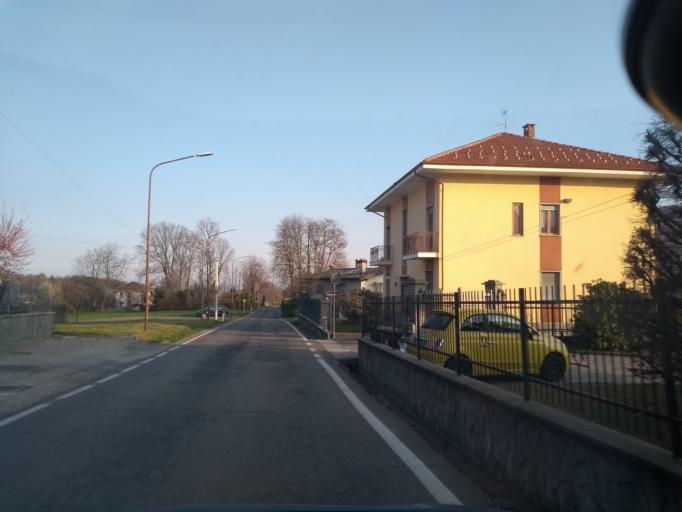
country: IT
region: Piedmont
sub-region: Provincia di Torino
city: Lanzo Torinese
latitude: 45.2851
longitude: 7.4823
